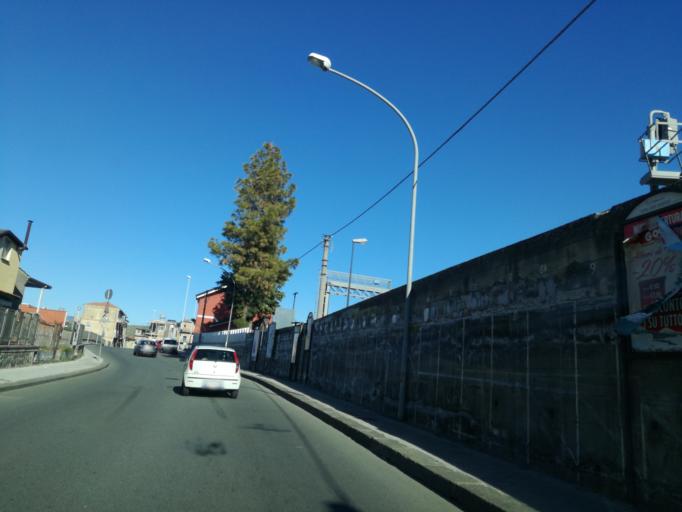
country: IT
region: Sicily
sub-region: Catania
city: Bronte
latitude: 37.7871
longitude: 14.8382
